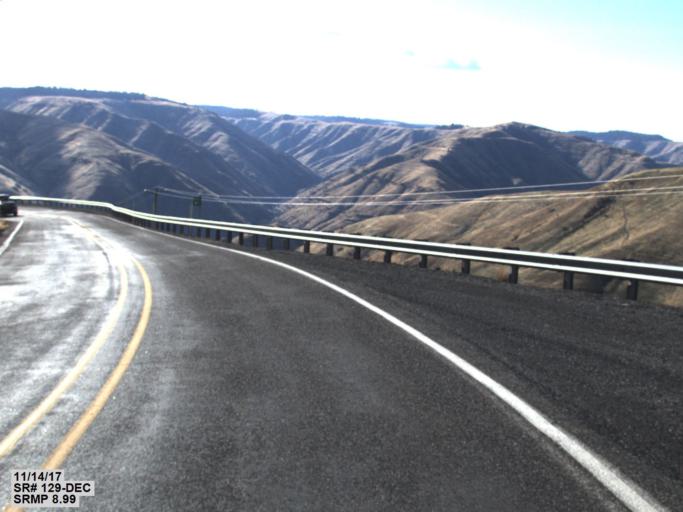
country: US
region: Washington
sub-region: Asotin County
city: Asotin
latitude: 46.0637
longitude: -117.2324
